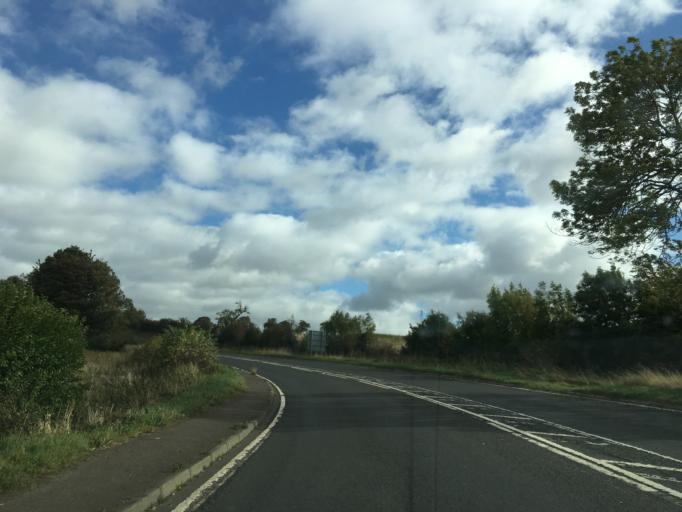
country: GB
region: Scotland
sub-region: Midlothian
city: Dalkeith
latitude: 55.8891
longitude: -3.0239
